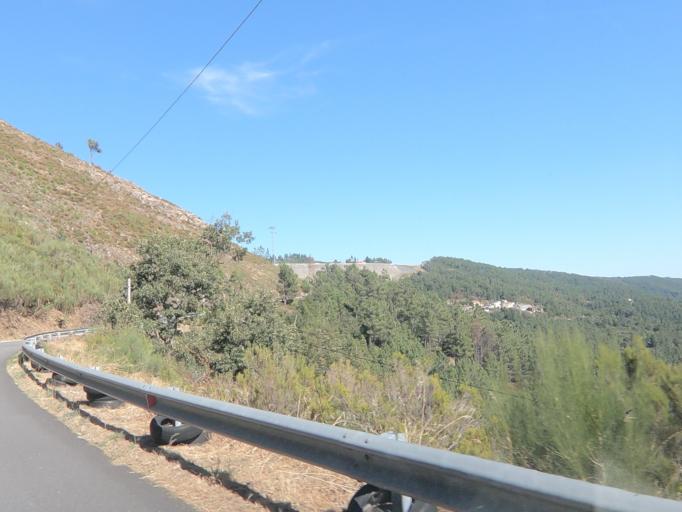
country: PT
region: Vila Real
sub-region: Santa Marta de Penaguiao
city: Santa Marta de Penaguiao
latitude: 41.2735
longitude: -7.8721
